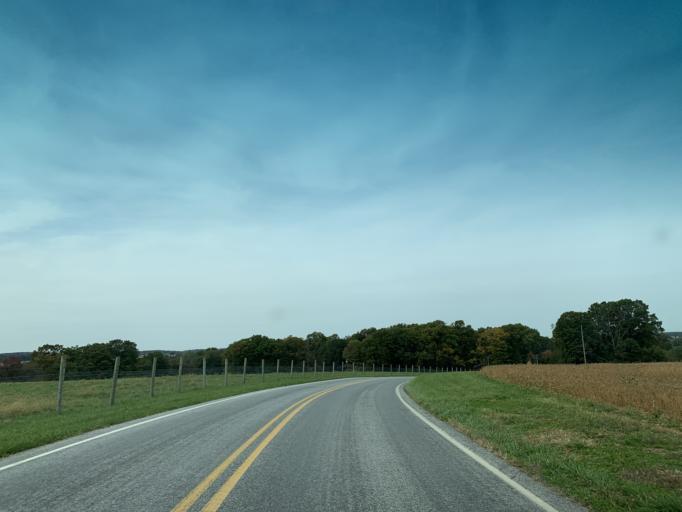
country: US
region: Pennsylvania
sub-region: York County
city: Windsor
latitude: 39.8684
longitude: -76.5126
